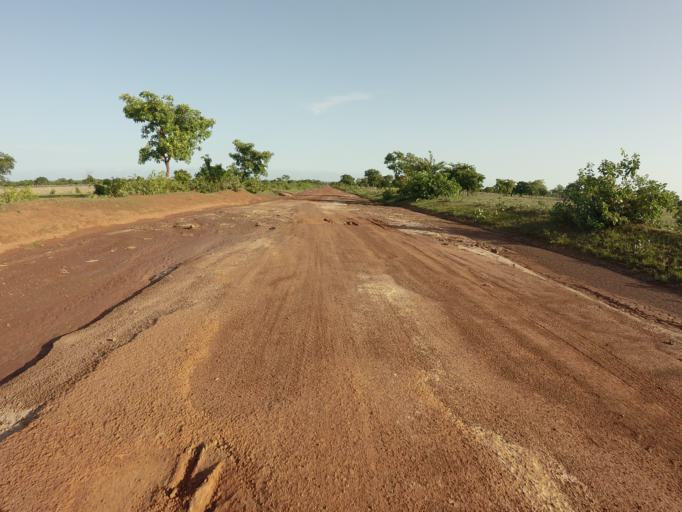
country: TG
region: Savanes
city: Sansanne-Mango
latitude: 10.3808
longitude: -0.0947
